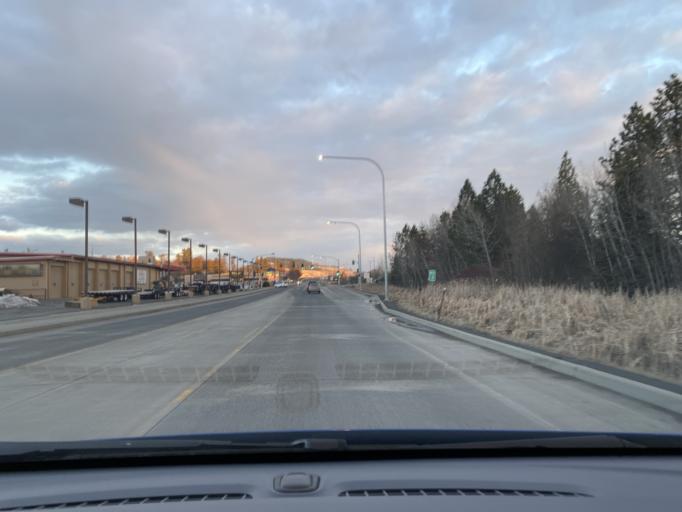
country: US
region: Idaho
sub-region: Latah County
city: Moscow
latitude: 46.7217
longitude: -116.9879
